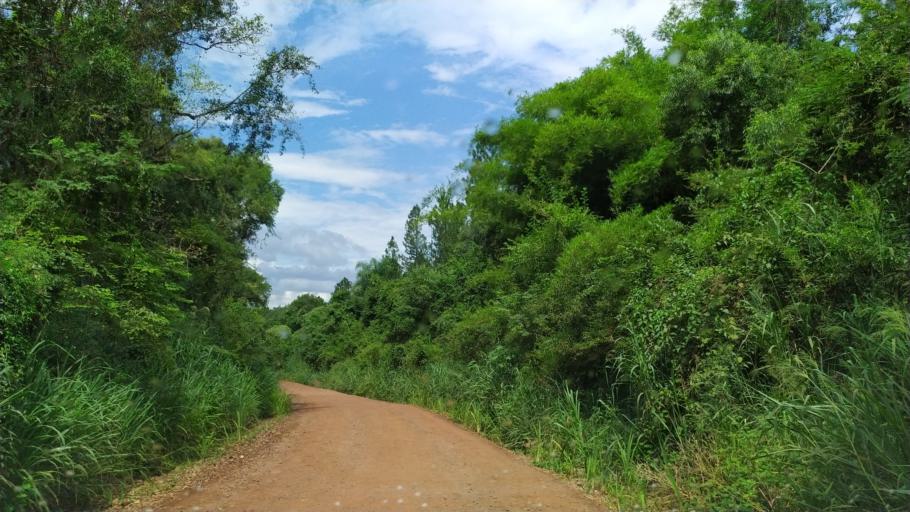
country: AR
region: Misiones
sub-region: Departamento de Eldorado
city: Eldorado
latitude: -26.4812
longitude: -54.5923
